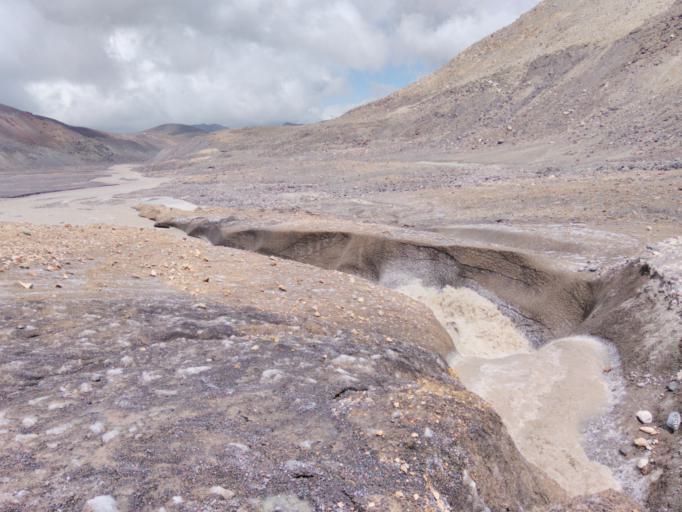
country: RU
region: Kabardino-Balkariya
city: Terskol
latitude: 43.3778
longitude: 42.5545
